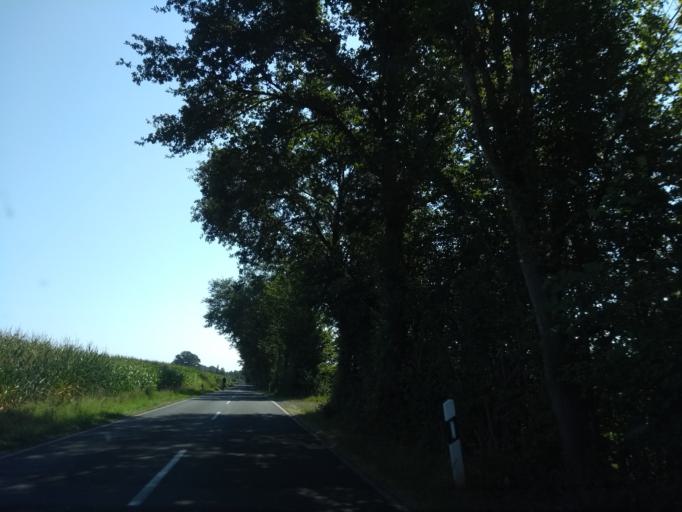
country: DE
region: North Rhine-Westphalia
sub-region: Regierungsbezirk Arnsberg
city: Lippstadt
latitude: 51.7235
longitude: 8.3921
